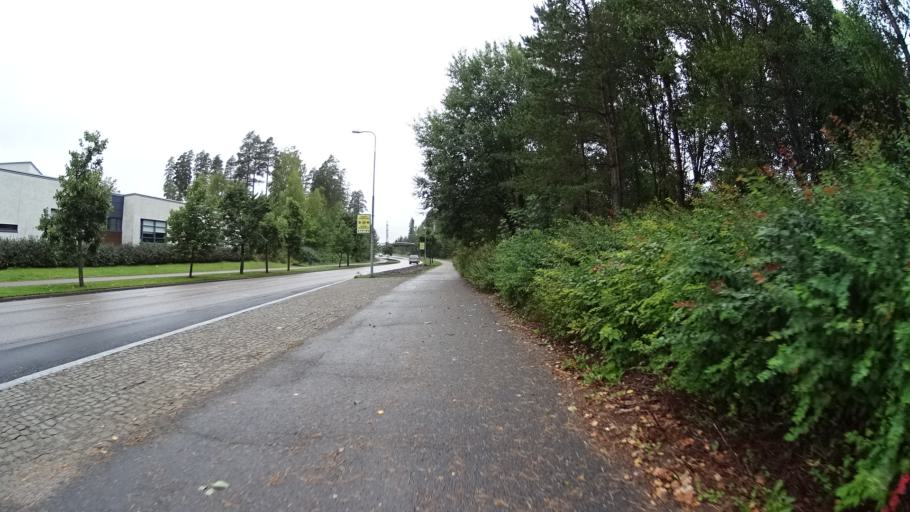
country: FI
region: Uusimaa
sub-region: Helsinki
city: Kauniainen
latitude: 60.2396
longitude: 24.7060
